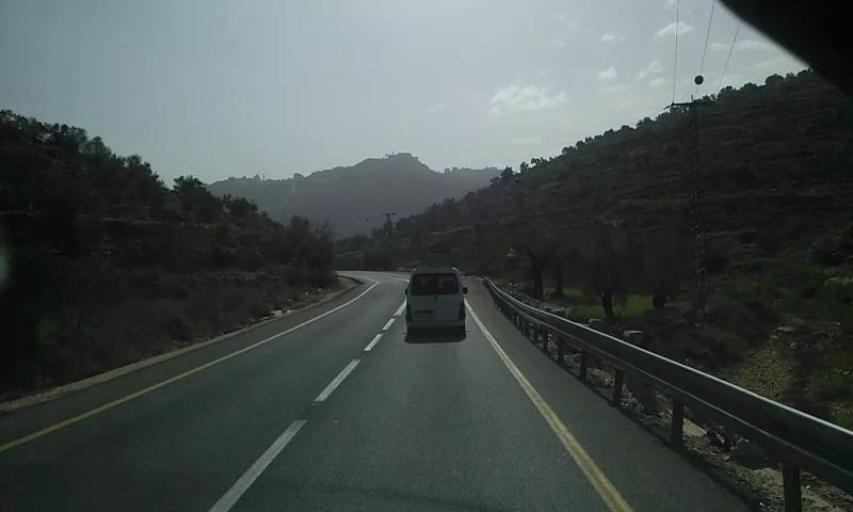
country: PS
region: West Bank
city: Silwad
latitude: 31.9943
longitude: 35.2456
